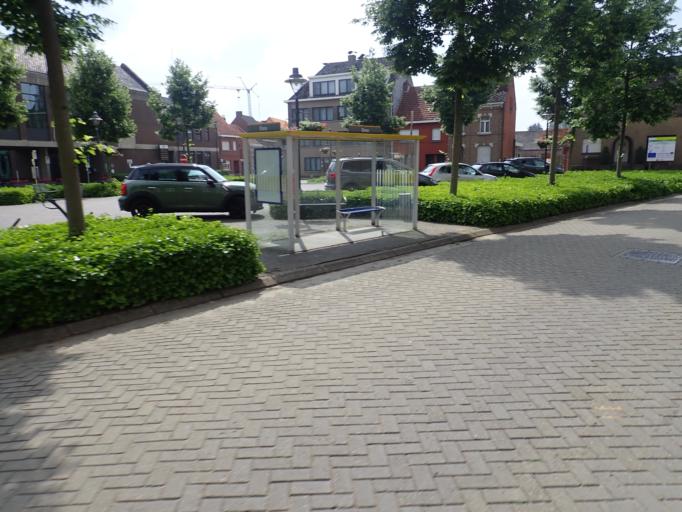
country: BE
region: Flanders
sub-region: Provincie Antwerpen
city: Vorselaar
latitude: 51.2019
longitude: 4.7729
